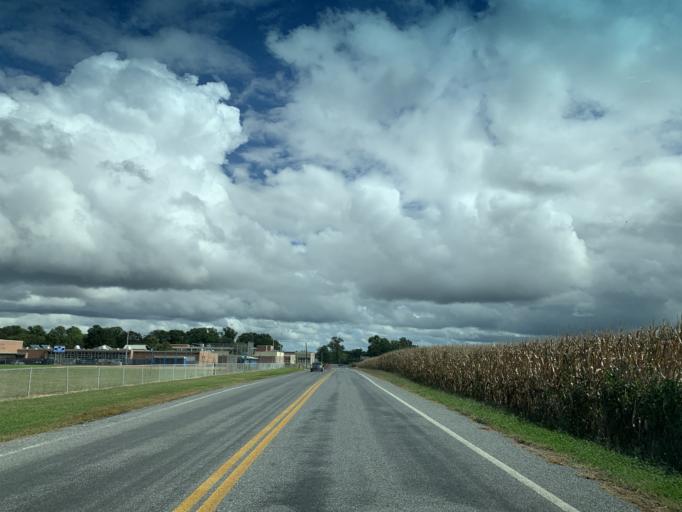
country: US
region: Maryland
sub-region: Caroline County
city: Denton
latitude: 38.9075
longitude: -75.8438
